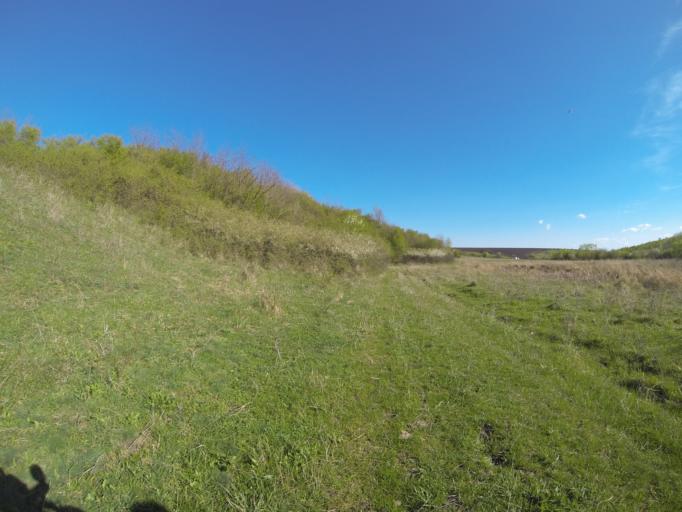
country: RO
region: Dolj
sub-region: Comuna Goesti
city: Goesti
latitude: 44.5028
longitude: 23.8007
